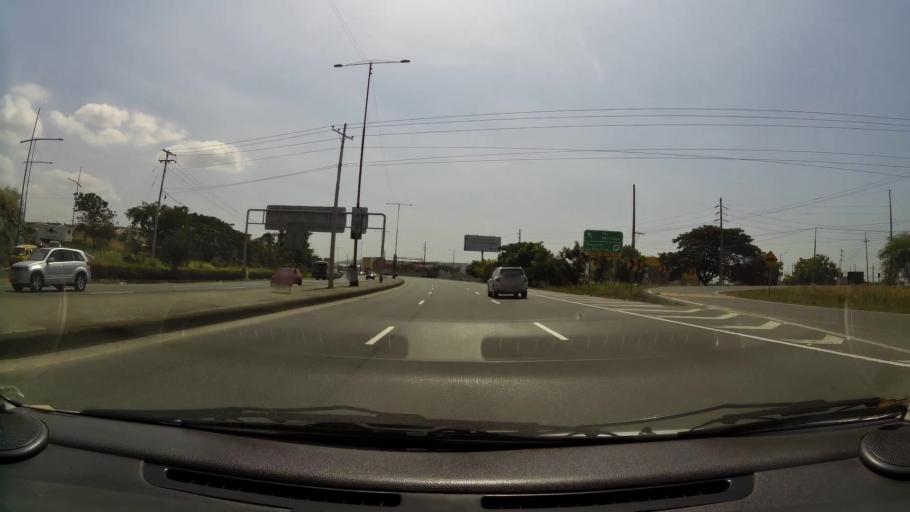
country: EC
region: Guayas
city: Eloy Alfaro
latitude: -2.0587
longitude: -79.8726
